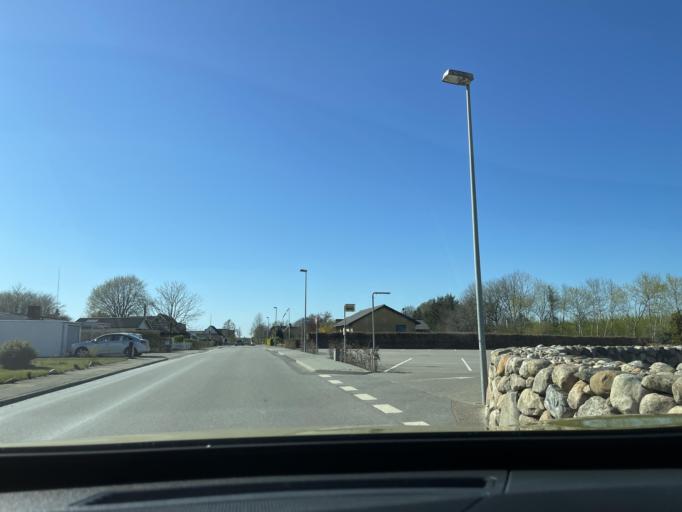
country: DK
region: Central Jutland
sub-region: Ikast-Brande Kommune
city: Bording Kirkeby
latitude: 56.1675
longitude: 9.2477
